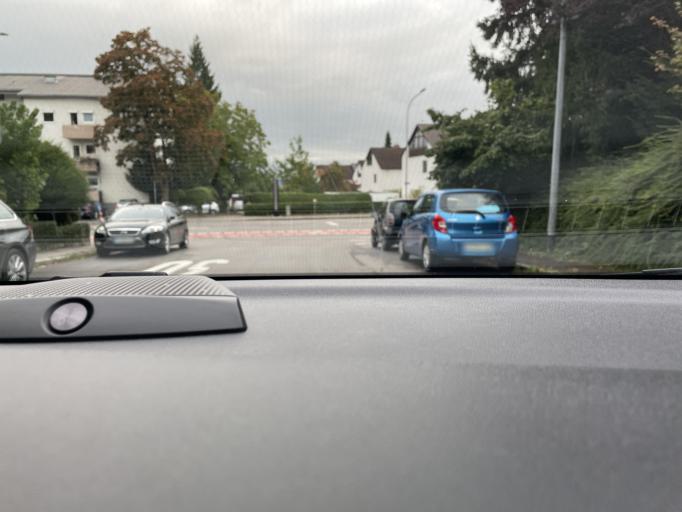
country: DE
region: Baden-Wuerttemberg
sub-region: Tuebingen Region
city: Friedrichshafen
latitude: 47.6569
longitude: 9.4592
